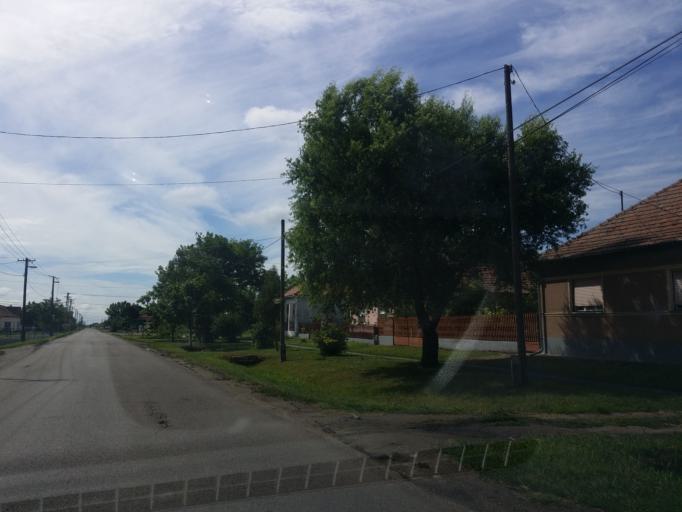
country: HU
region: Heves
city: Tiszanana
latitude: 47.6016
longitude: 20.4445
